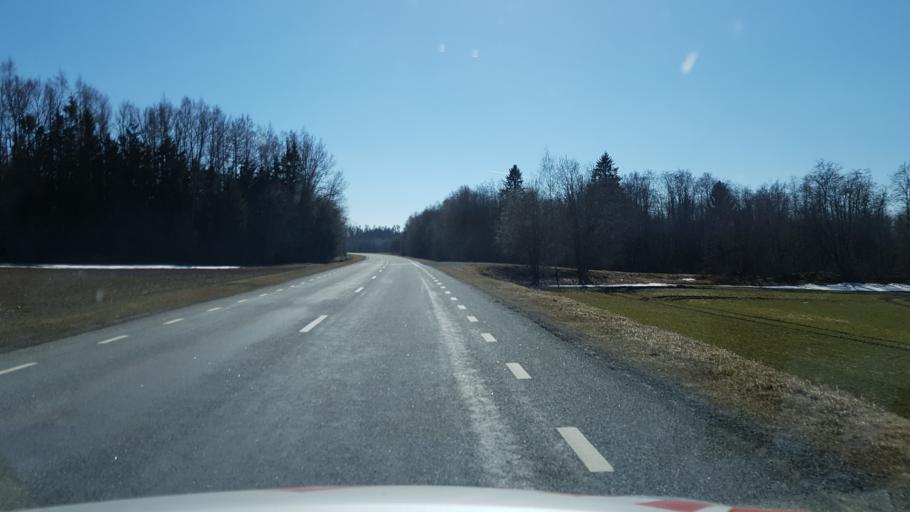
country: EE
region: Jaervamaa
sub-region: Jaerva-Jaani vald
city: Jarva-Jaani
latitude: 59.0973
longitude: 25.9820
